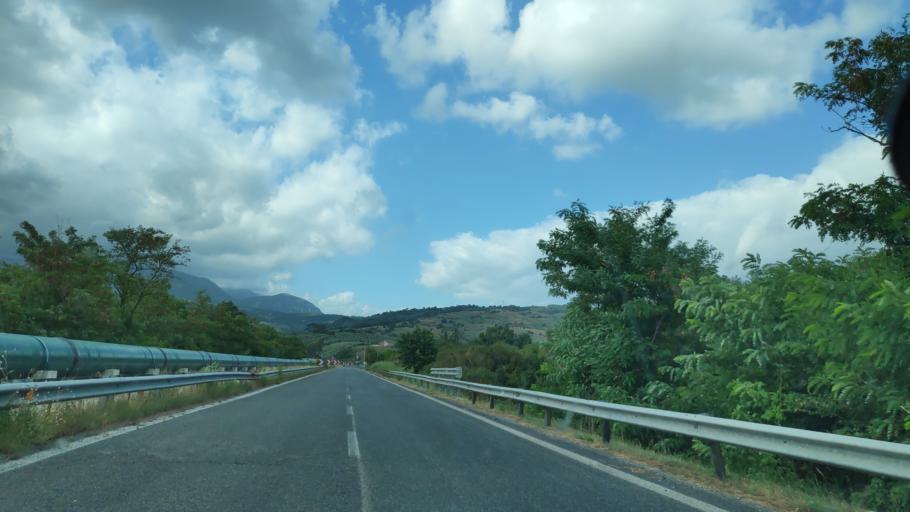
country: IT
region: Campania
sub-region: Provincia di Salerno
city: Serre
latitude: 40.6195
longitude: 15.1813
